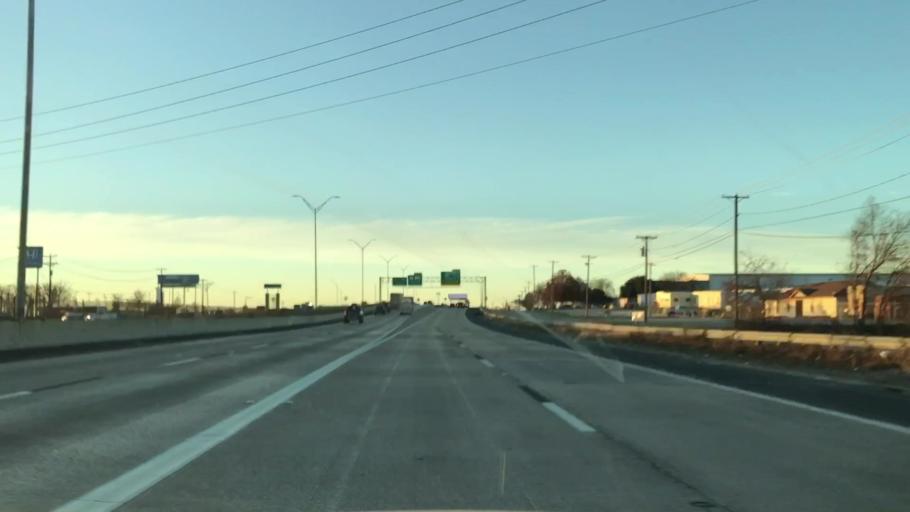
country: US
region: Texas
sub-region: Johnson County
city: Burleson
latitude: 32.5578
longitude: -97.3192
